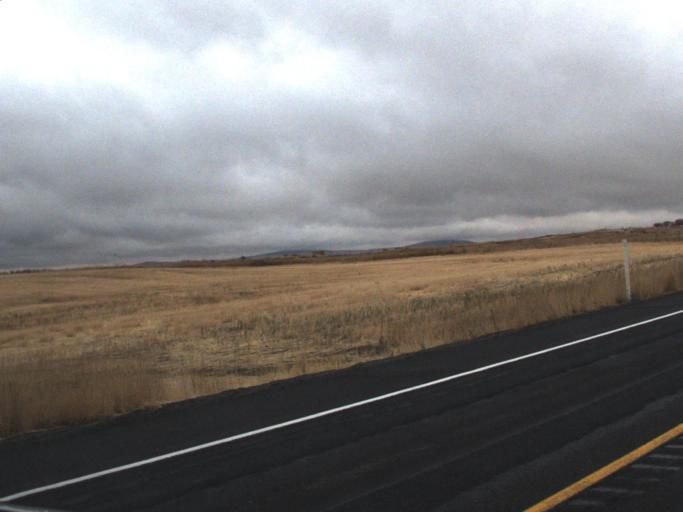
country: US
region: Washington
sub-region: Spokane County
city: Medical Lake
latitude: 47.6428
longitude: -117.7547
